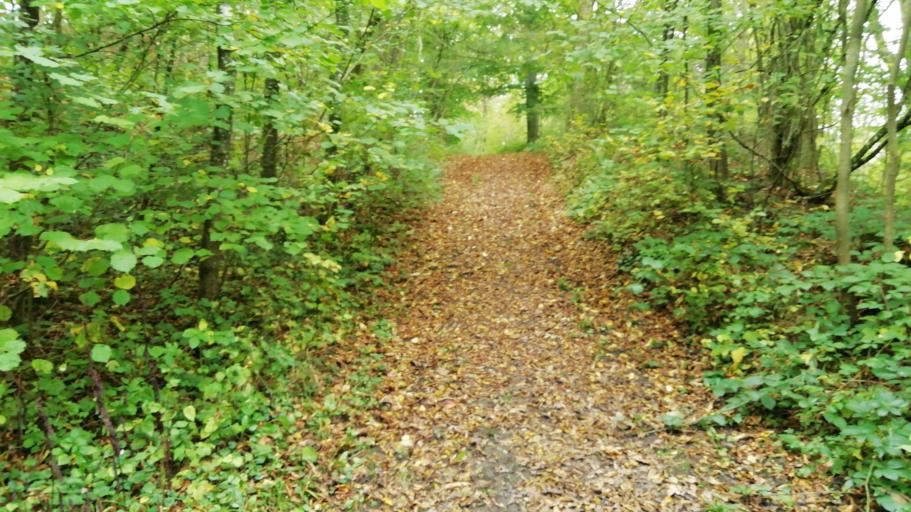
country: FR
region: Nord-Pas-de-Calais
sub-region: Departement du Nord
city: Trelon
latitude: 50.1132
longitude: 4.0913
